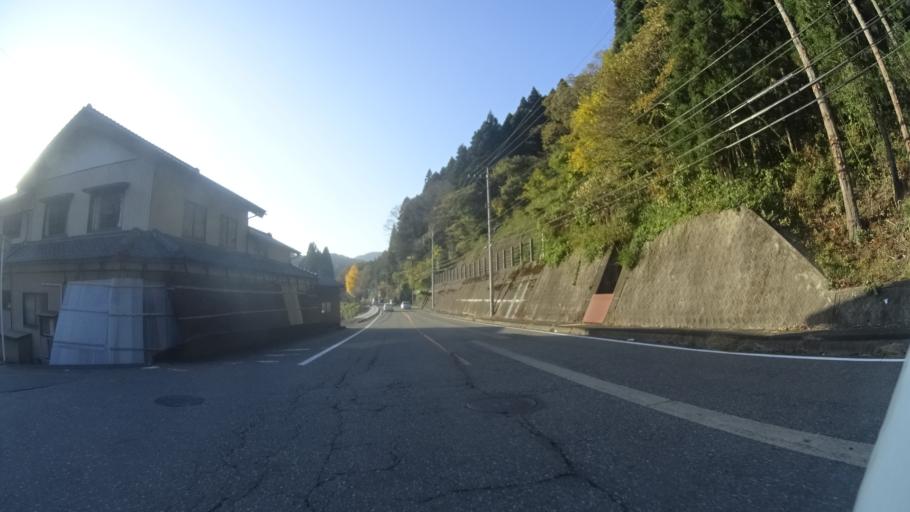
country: JP
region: Fukui
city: Ono
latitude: 35.9997
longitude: 136.4190
